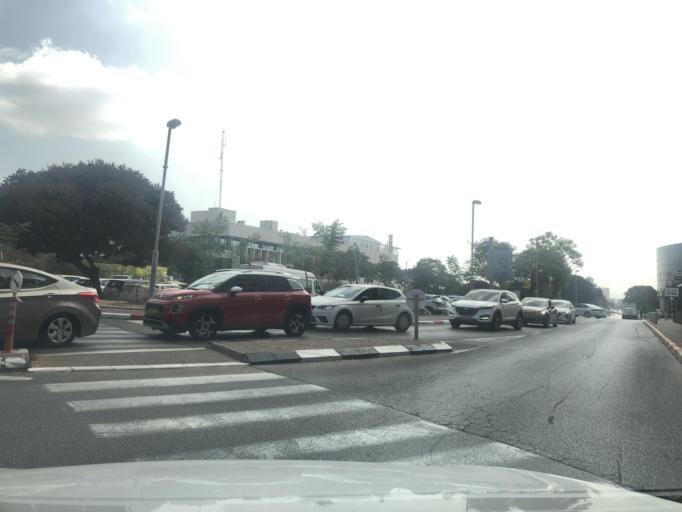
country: IL
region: Tel Aviv
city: Or Yehuda
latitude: 32.0470
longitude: 34.8459
